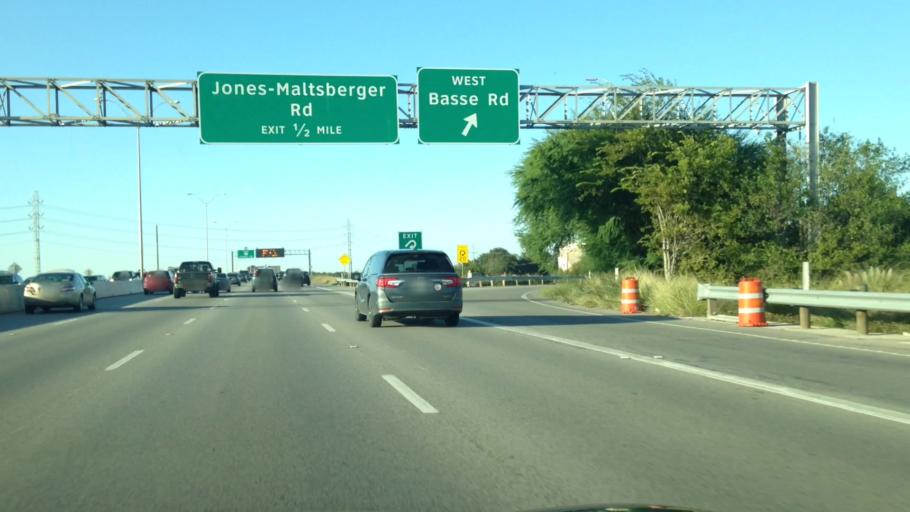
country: US
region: Texas
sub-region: Bexar County
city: Olmos Park
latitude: 29.4915
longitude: -98.4835
